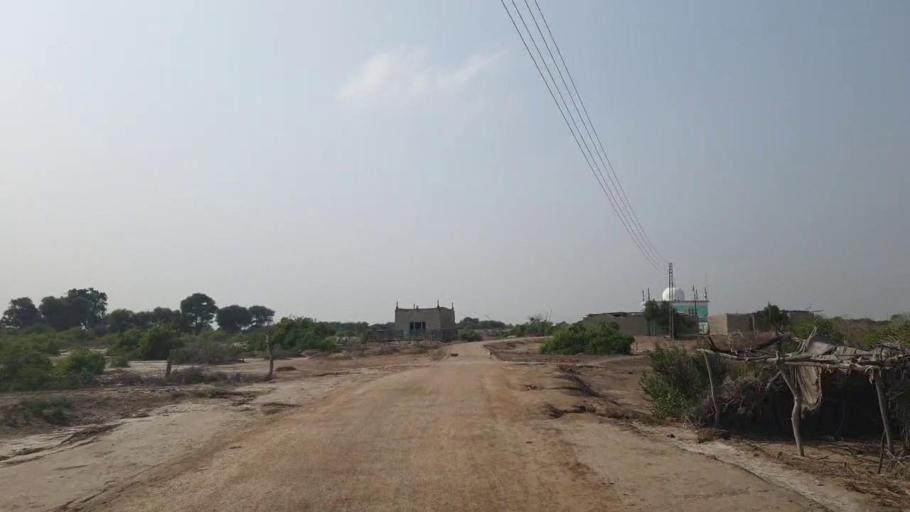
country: PK
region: Sindh
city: Badin
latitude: 24.5454
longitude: 68.6527
